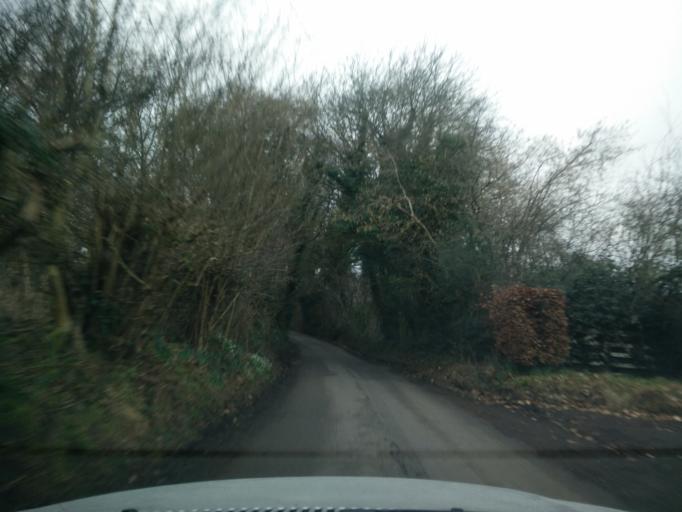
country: GB
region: England
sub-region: Buckinghamshire
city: Great Missenden
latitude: 51.6700
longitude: -0.6853
